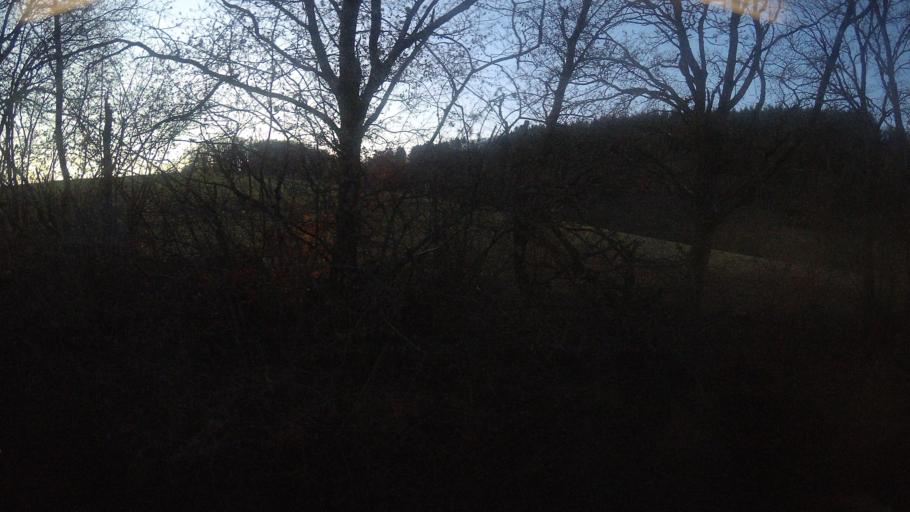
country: DE
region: Rheinland-Pfalz
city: Herchweiler
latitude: 49.5019
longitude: 7.2638
